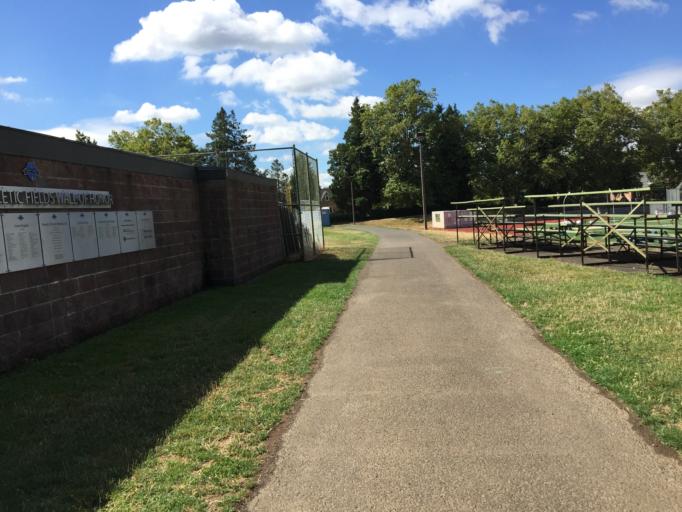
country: US
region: Oregon
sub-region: Multnomah County
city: Portland
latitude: 45.5388
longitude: -122.6289
